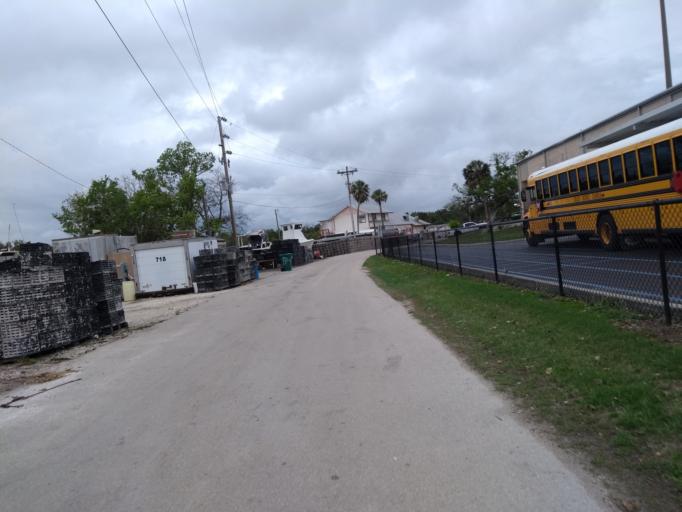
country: US
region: Florida
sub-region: Collier County
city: Marco
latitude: 25.8633
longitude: -81.3870
